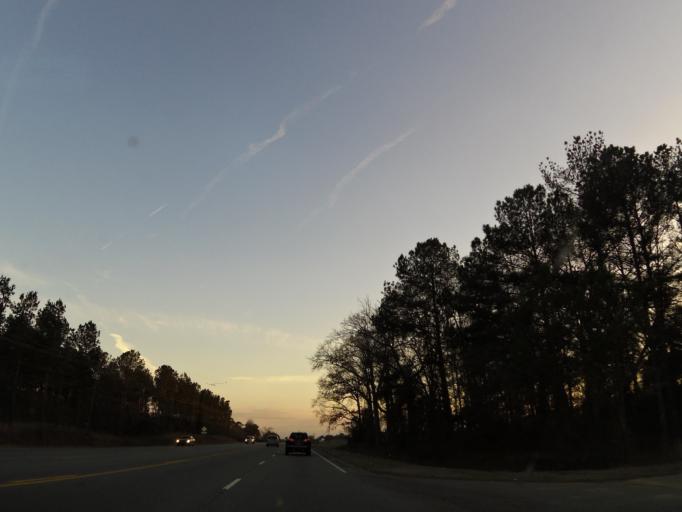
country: US
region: Georgia
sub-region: Lee County
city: Leesburg
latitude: 31.6655
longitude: -84.1729
